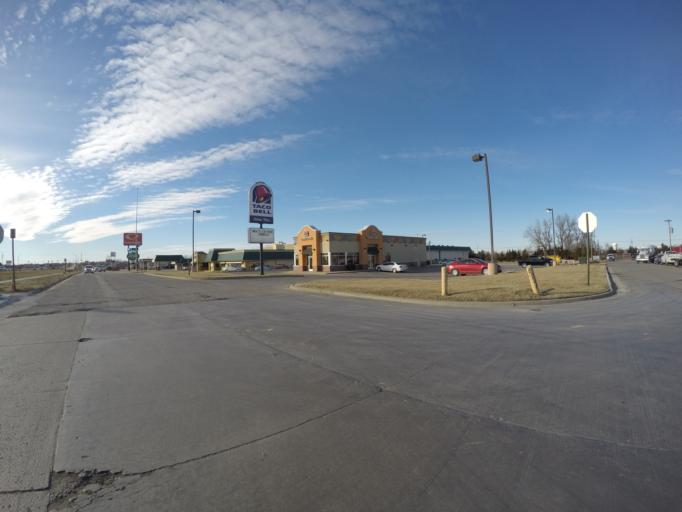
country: US
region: Kansas
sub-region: McPherson County
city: McPherson
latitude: 38.3712
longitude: -97.6267
